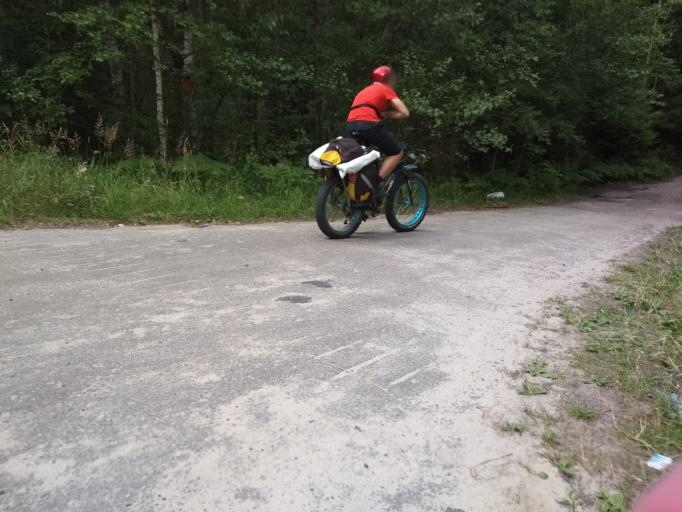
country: RU
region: Moskovskaya
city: Misheronskiy
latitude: 55.6160
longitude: 39.7232
